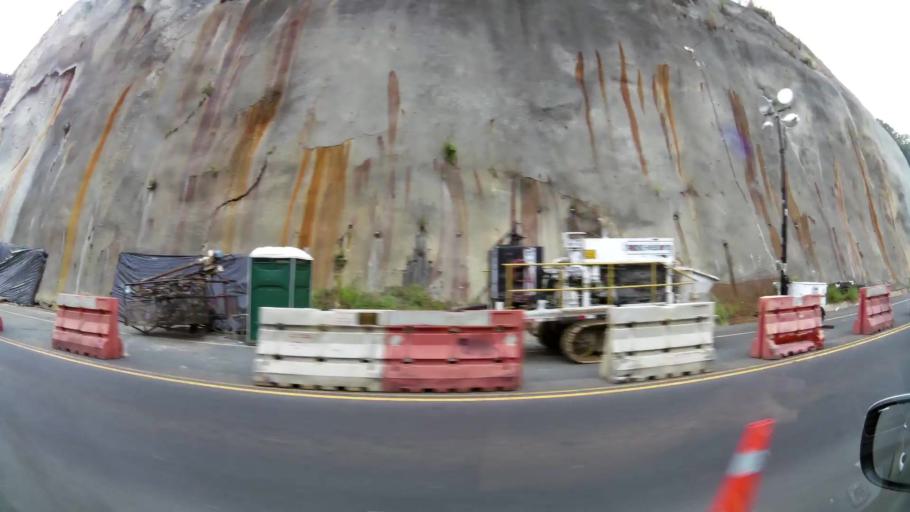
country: CR
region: Alajuela
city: Atenas
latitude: 9.9352
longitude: -84.4072
